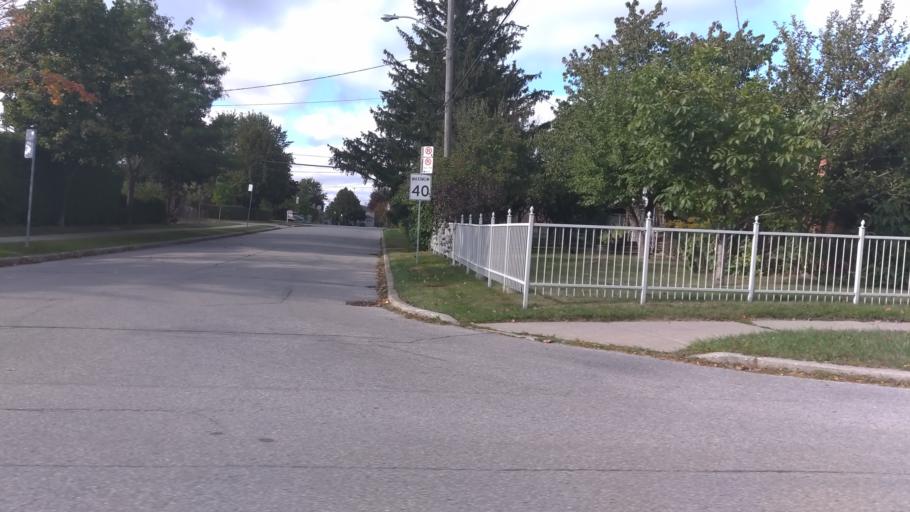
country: CA
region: Ontario
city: Toronto
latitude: 43.7210
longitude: -79.4600
